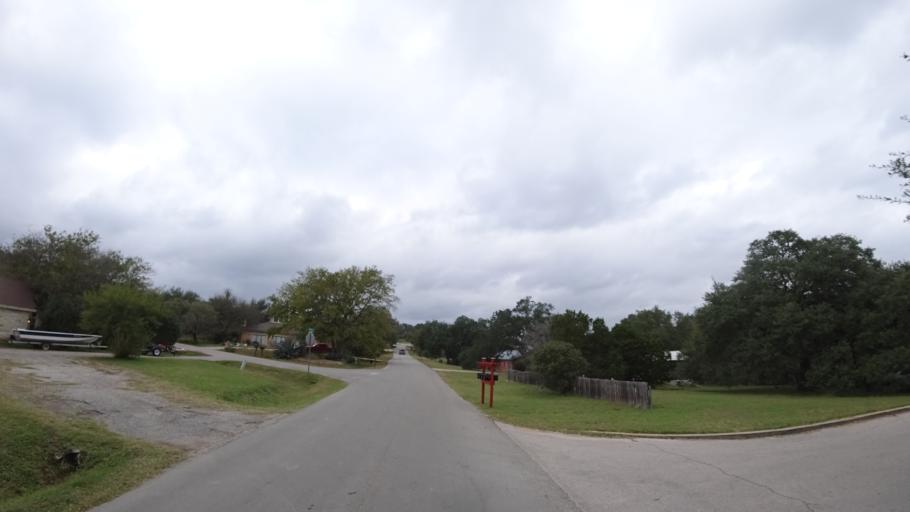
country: US
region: Texas
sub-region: Travis County
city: Bee Cave
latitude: 30.3294
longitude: -97.9200
